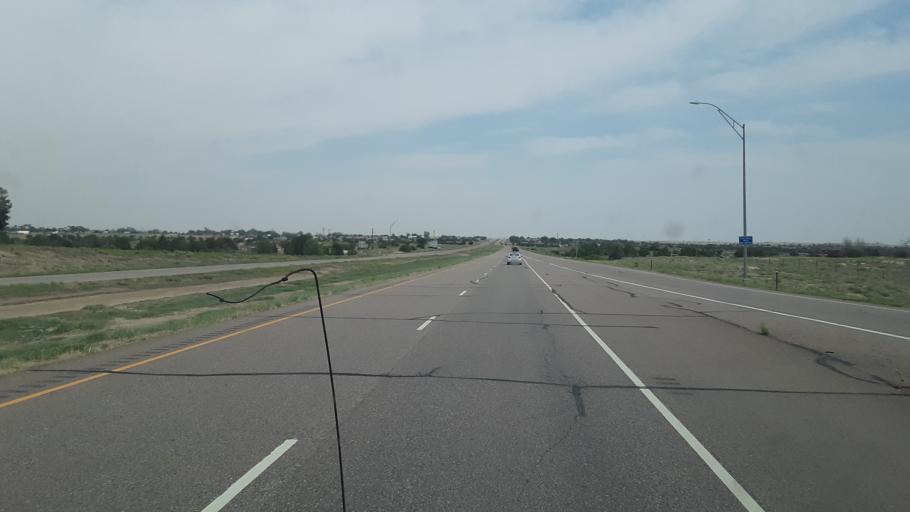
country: US
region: Colorado
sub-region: Fremont County
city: Penrose
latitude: 38.4178
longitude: -105.0395
